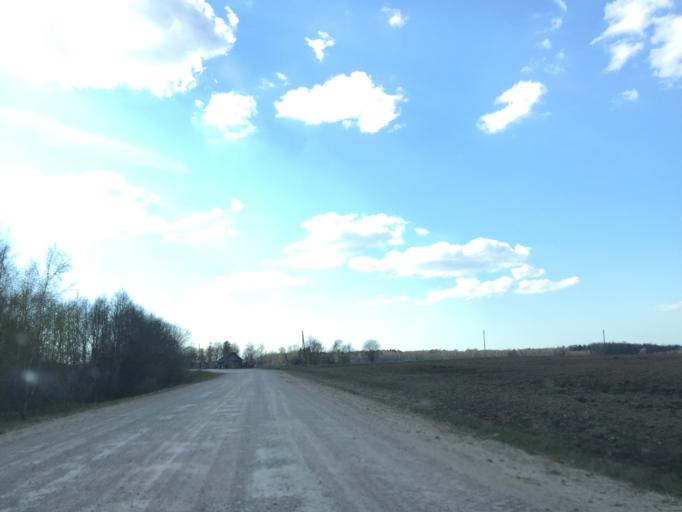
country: LV
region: Krimulda
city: Ragana
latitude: 57.3396
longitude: 24.6264
